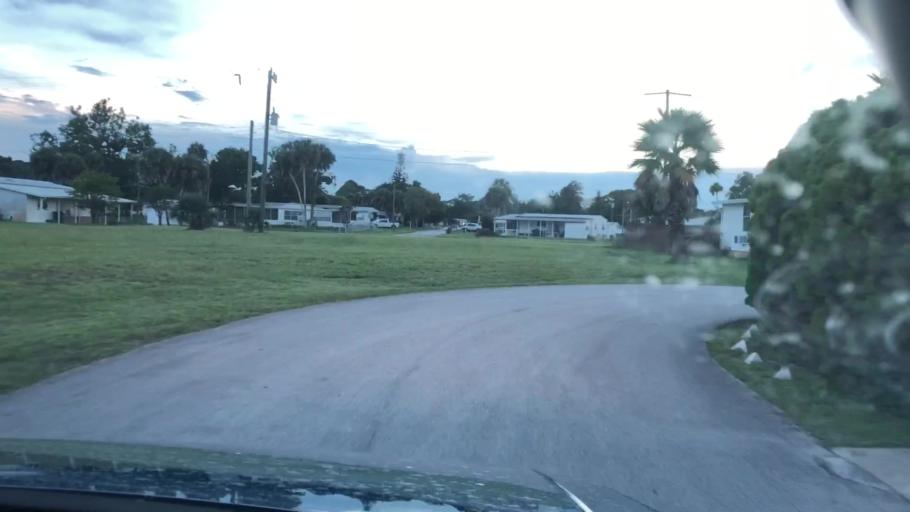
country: US
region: Florida
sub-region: Volusia County
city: Oak Hill
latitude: 28.9142
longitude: -80.8623
